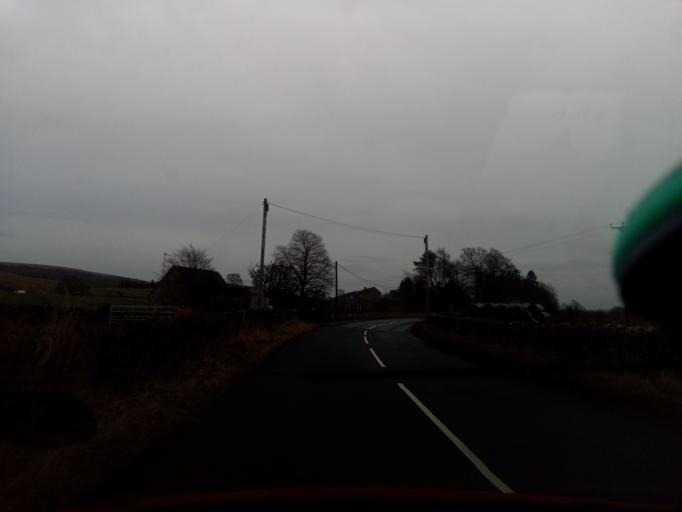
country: GB
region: England
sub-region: Northumberland
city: Rochester
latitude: 55.1599
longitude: -2.3045
